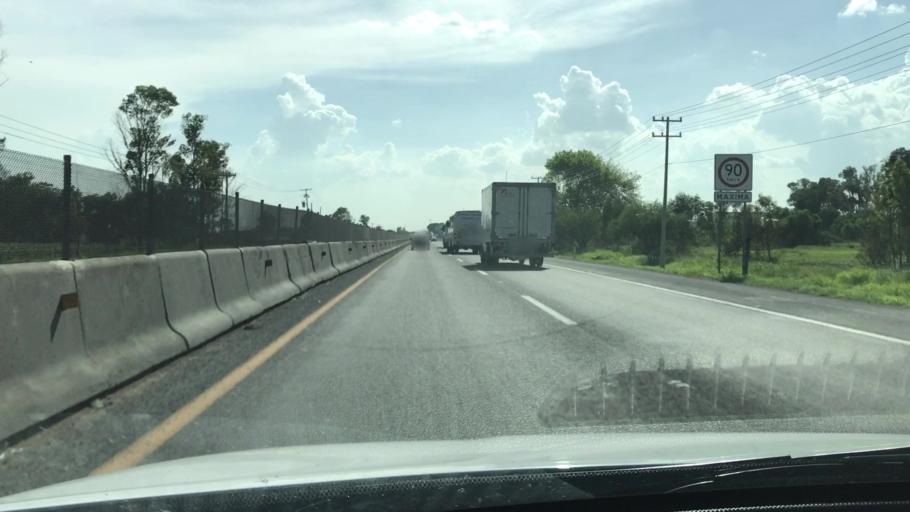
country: MX
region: Guanajuato
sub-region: Villagran
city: El Chinaco (El Pujido)
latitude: 20.5141
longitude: -100.9125
